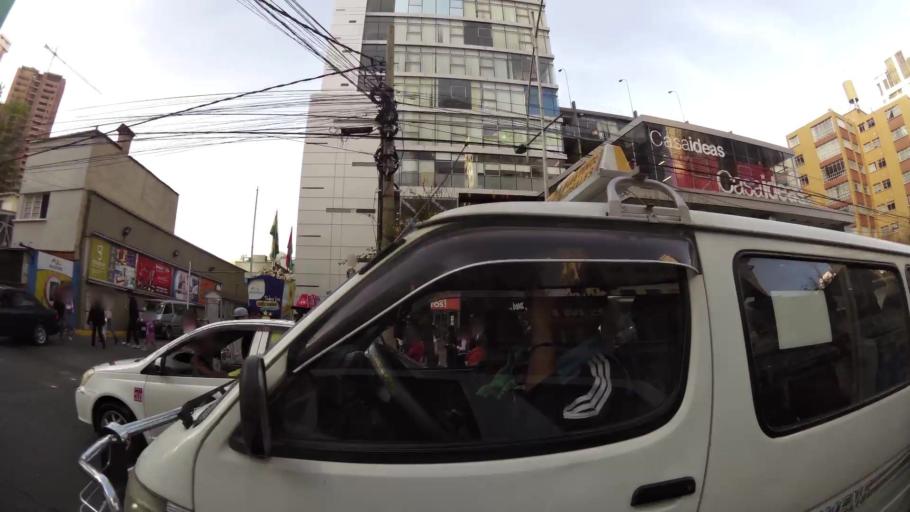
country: BO
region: La Paz
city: La Paz
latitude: -16.5111
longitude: -68.1226
